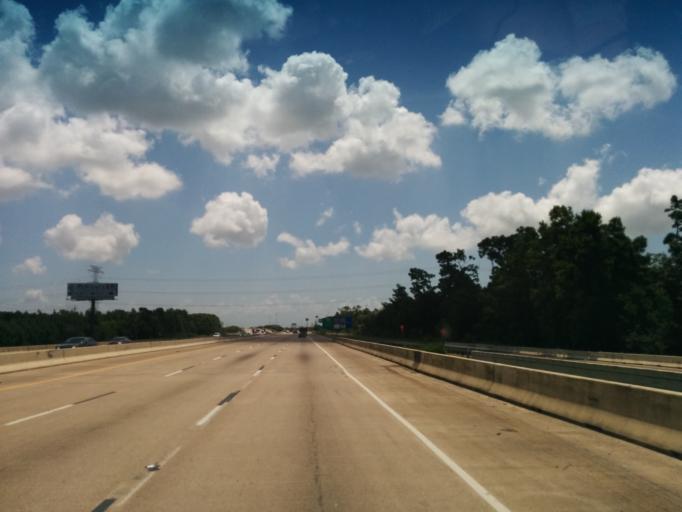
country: US
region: Texas
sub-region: Chambers County
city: Mont Belvieu
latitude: 29.8210
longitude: -94.9101
